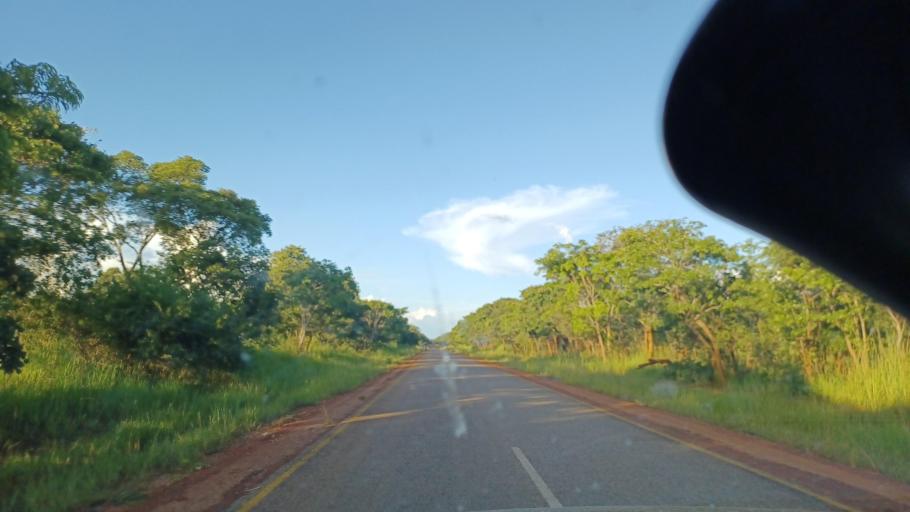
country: ZM
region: North-Western
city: Kalengwa
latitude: -13.1381
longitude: 25.0715
